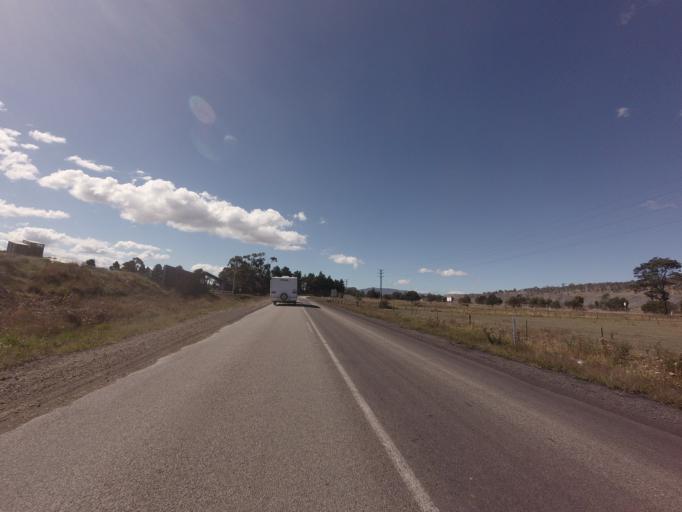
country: AU
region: Tasmania
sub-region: Break O'Day
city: St Helens
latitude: -41.6318
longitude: 147.9851
